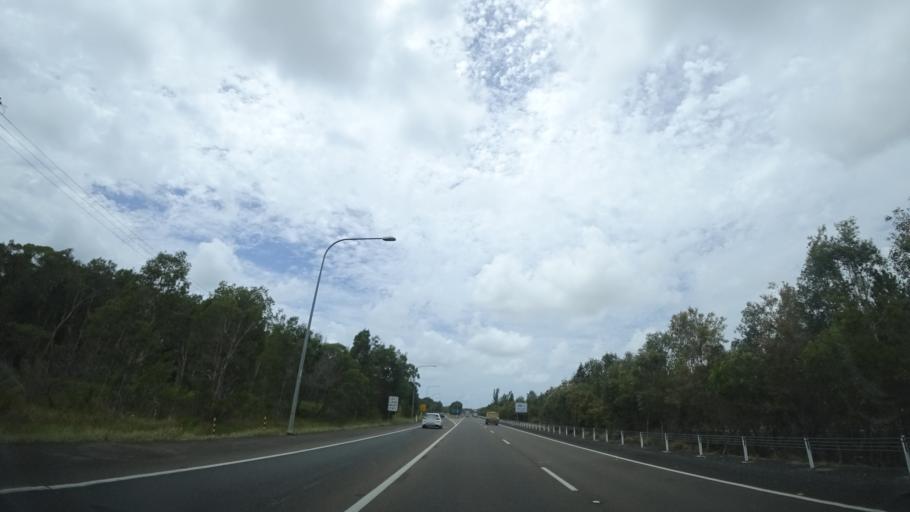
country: AU
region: Queensland
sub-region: Sunshine Coast
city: Mooloolaba
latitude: -26.6866
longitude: 153.1060
